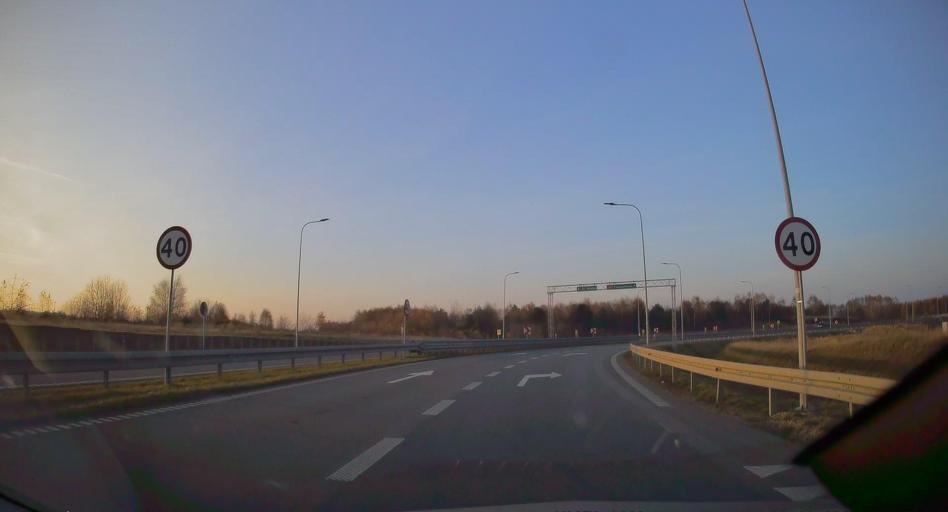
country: PL
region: Silesian Voivodeship
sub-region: Powiat klobucki
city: Kamyk
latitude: 50.8497
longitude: 19.0365
